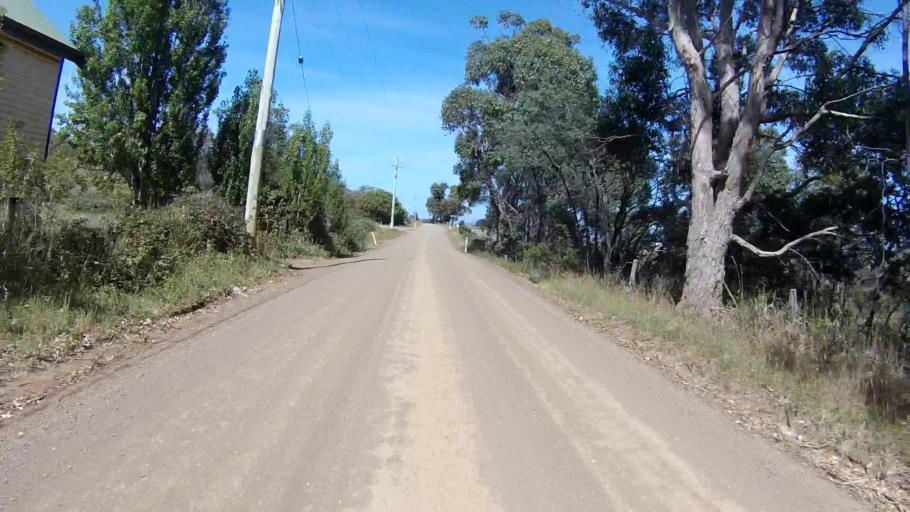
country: AU
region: Tasmania
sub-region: Sorell
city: Sorell
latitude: -42.7338
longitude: 147.5929
